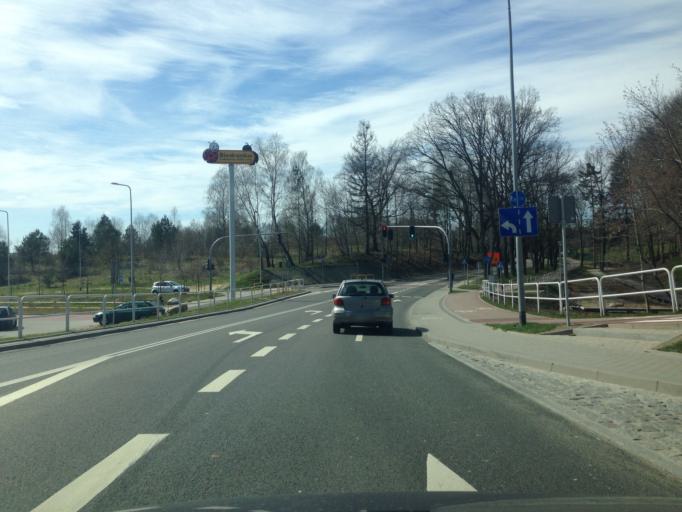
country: PL
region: Pomeranian Voivodeship
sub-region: Gdynia
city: Wielki Kack
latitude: 54.5001
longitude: 18.4569
